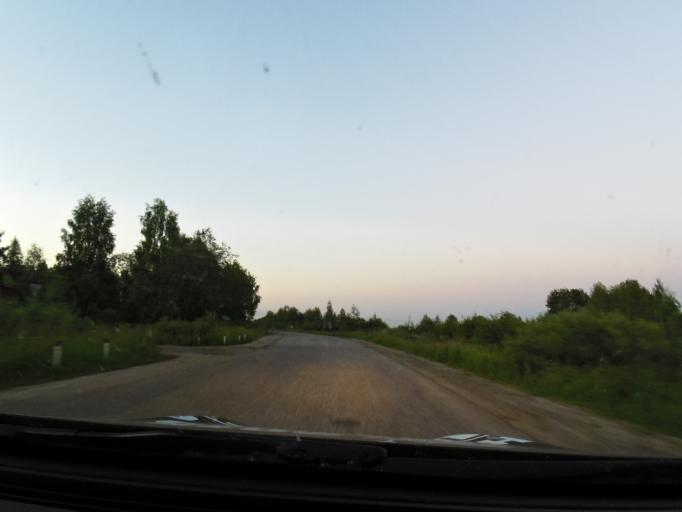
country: RU
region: Kostroma
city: Buy
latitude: 58.4830
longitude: 41.4900
